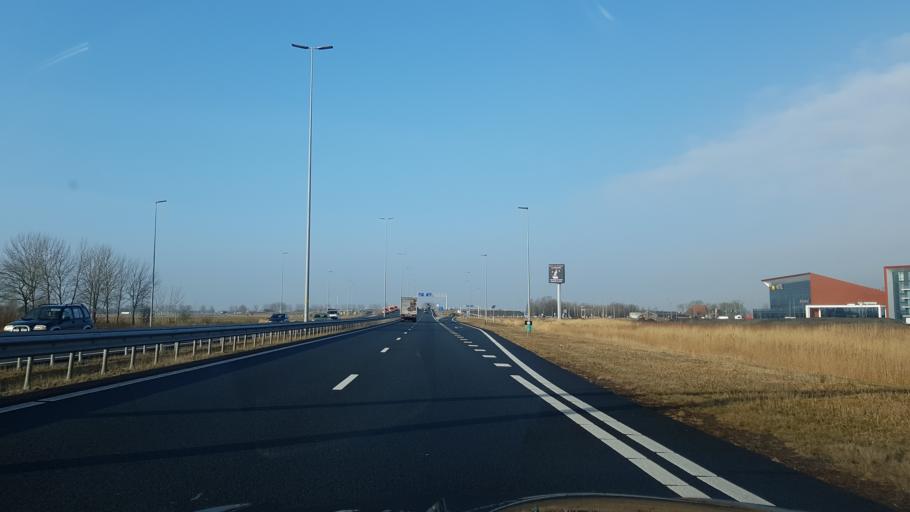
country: NL
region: Friesland
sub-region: Gemeente Leeuwarden
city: Wirdum
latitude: 53.1613
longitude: 5.8048
